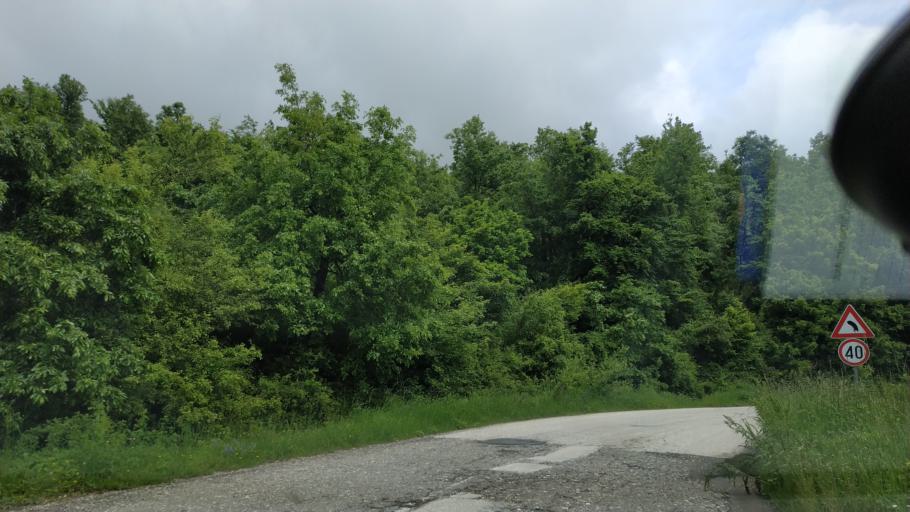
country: RS
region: Central Serbia
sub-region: Zajecarski Okrug
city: Soko Banja
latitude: 43.7186
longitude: 21.9445
